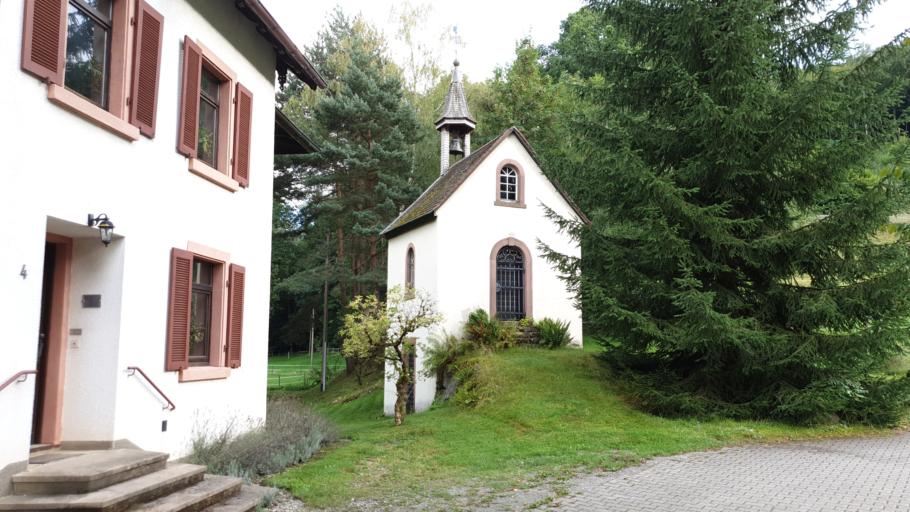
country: DE
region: Baden-Wuerttemberg
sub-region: Freiburg Region
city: Oberried
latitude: 47.9423
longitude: 7.9491
